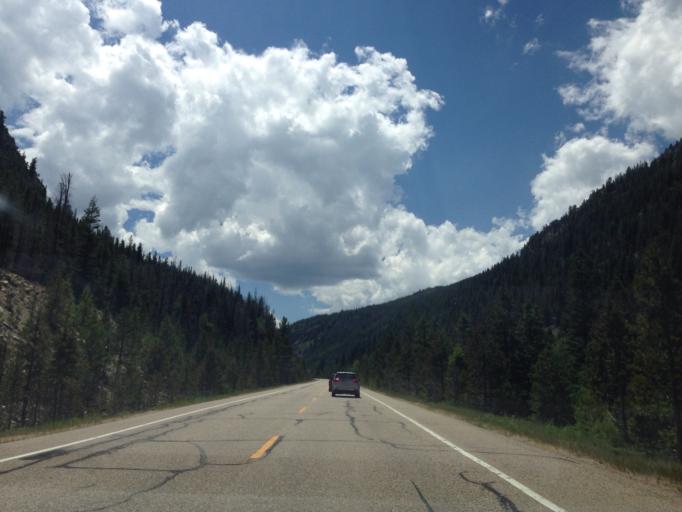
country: US
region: Colorado
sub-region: Larimer County
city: Estes Park
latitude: 40.6331
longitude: -105.8089
